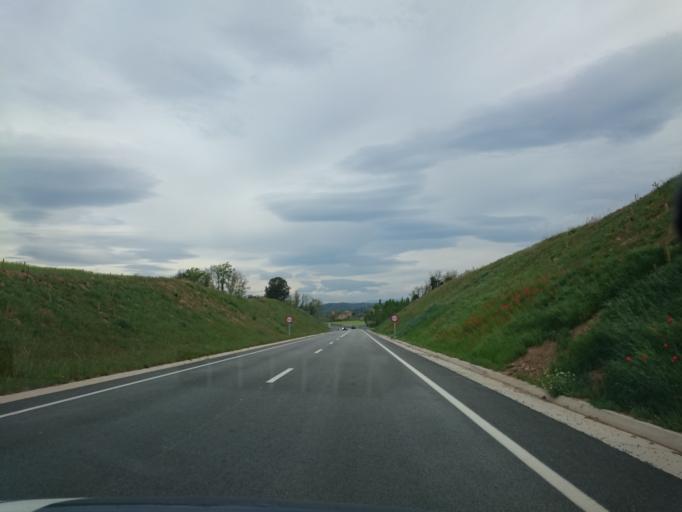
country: ES
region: Catalonia
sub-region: Provincia de Barcelona
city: Olost
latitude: 41.9846
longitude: 2.1035
